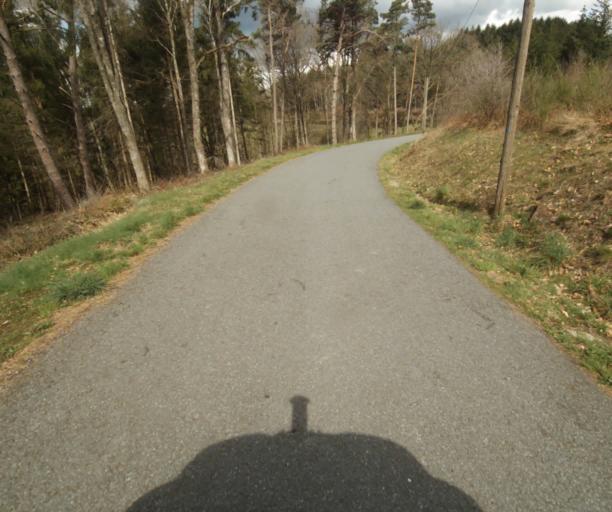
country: FR
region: Limousin
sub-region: Departement de la Correze
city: Correze
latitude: 45.3881
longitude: 1.9169
